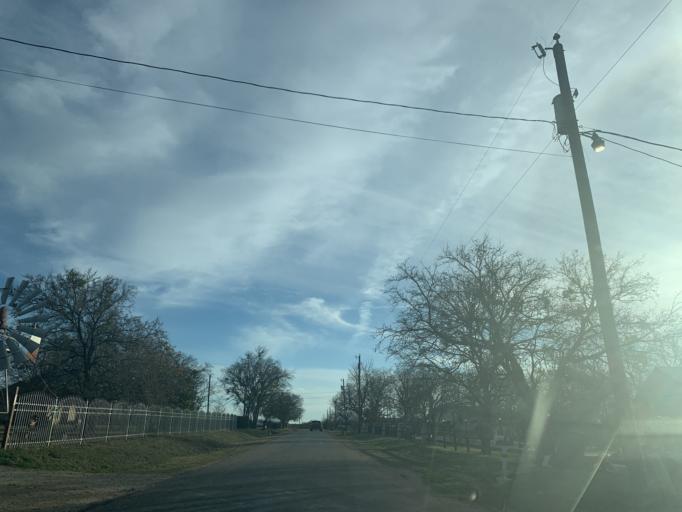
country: US
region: Texas
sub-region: Bell County
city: Salado
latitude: 30.8831
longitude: -97.5806
